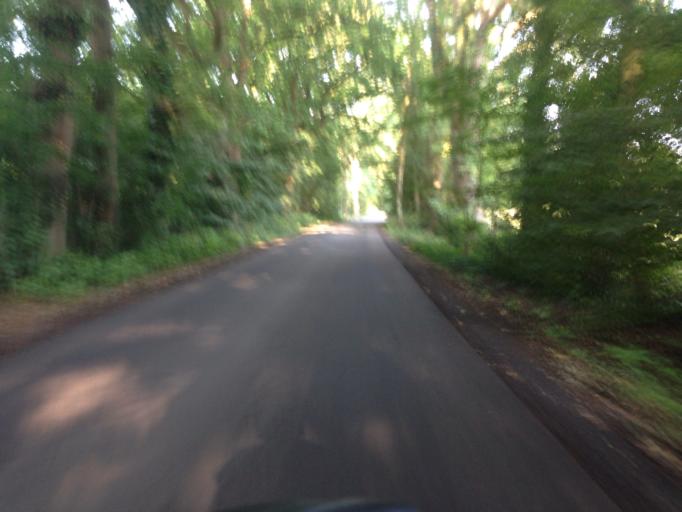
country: DE
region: North Rhine-Westphalia
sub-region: Regierungsbezirk Munster
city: Muenster
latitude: 51.9873
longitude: 7.6016
